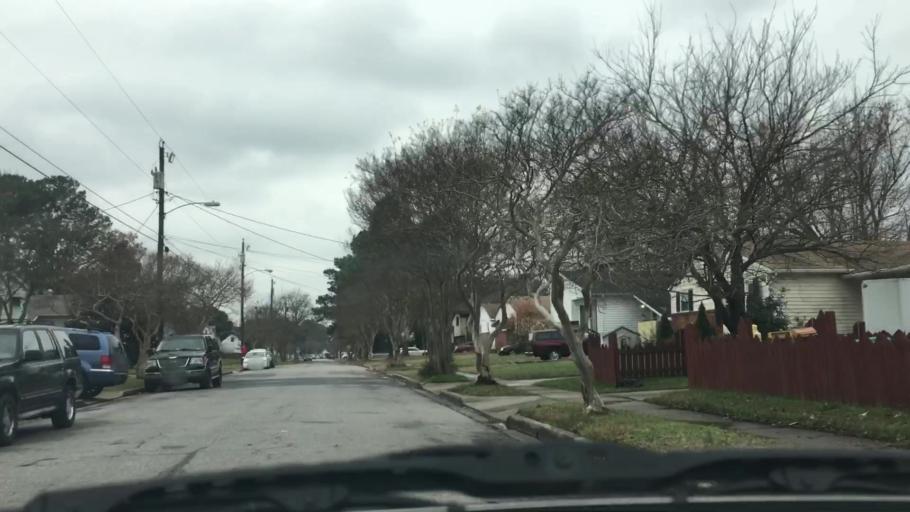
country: US
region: Virginia
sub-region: City of Norfolk
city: Norfolk
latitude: 36.8750
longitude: -76.2370
